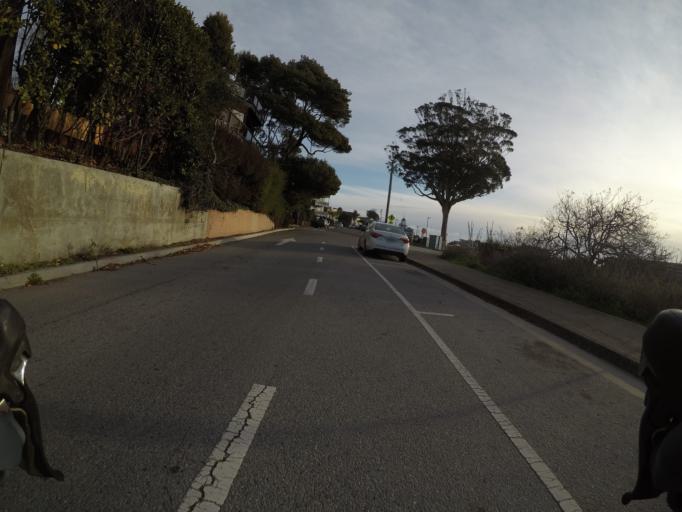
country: US
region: California
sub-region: Santa Cruz County
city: Twin Lakes
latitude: 36.9657
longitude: -122.0008
